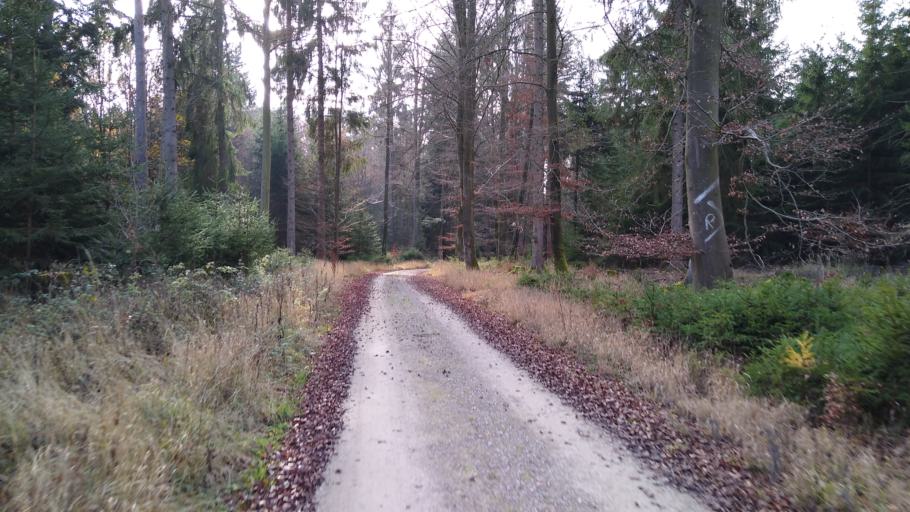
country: DE
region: Bavaria
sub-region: Upper Palatinate
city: Seubersdorf
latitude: 49.1382
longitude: 11.6338
